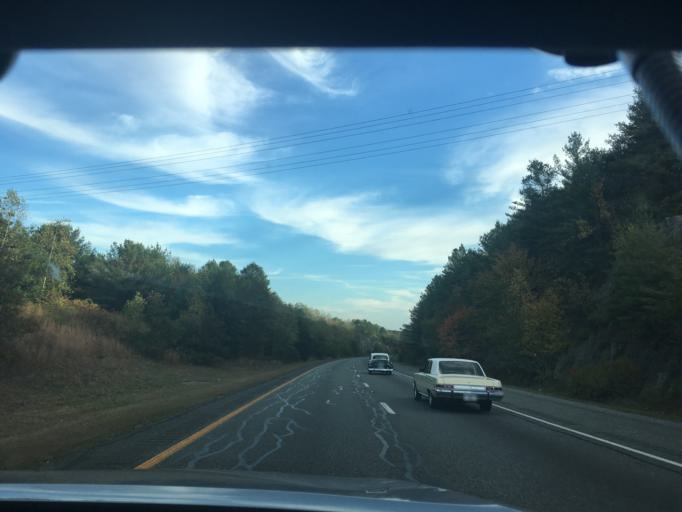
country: US
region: Rhode Island
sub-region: Providence County
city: Johnston
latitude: 41.7735
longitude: -71.4899
